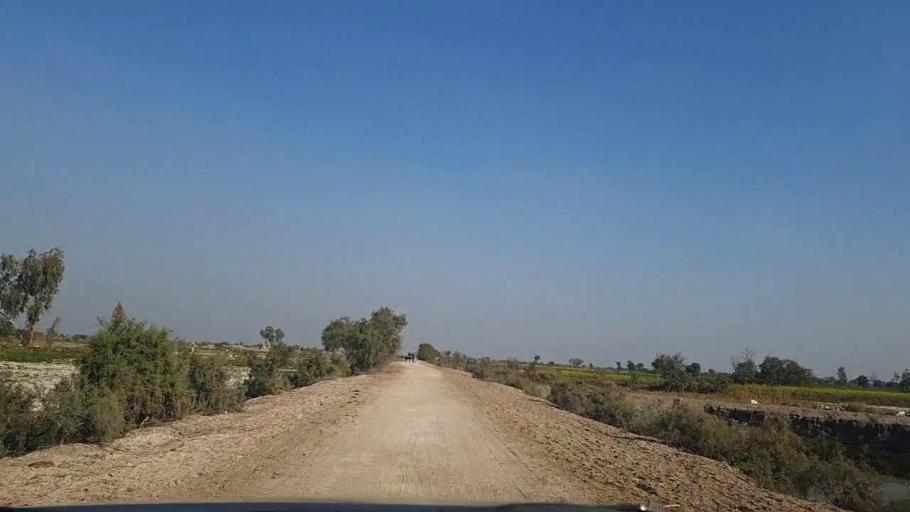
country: PK
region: Sindh
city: Daur
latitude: 26.3178
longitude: 68.1800
